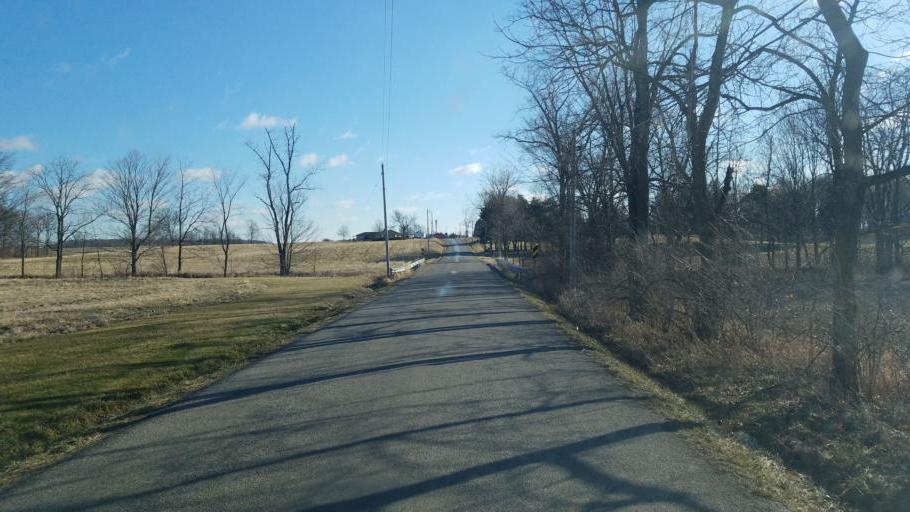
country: US
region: Ohio
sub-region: Morrow County
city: Mount Gilead
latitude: 40.5160
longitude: -82.8305
